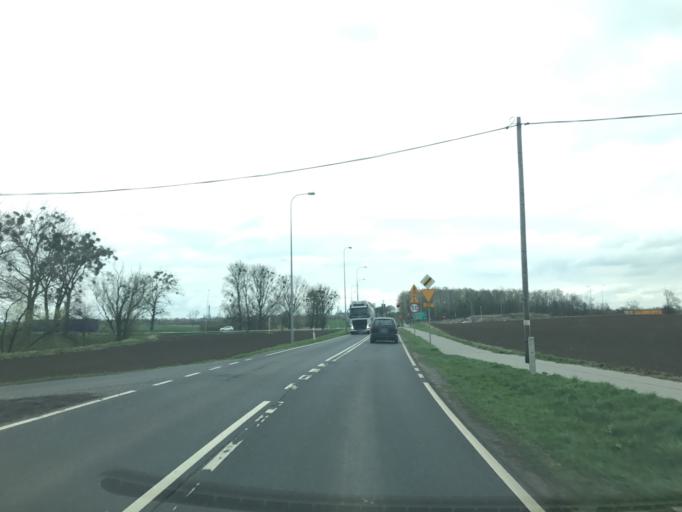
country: PL
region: Kujawsko-Pomorskie
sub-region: Powiat torunski
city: Chelmza
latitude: 53.1809
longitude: 18.5639
